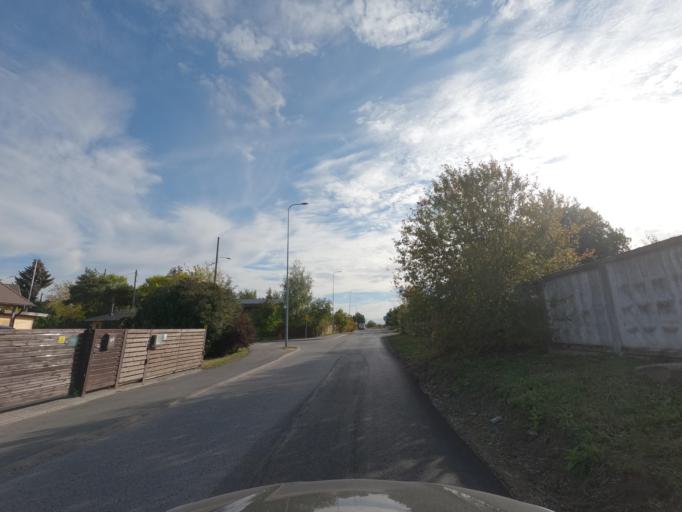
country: EE
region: Harju
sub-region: Saue vald
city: Laagri
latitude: 59.3482
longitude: 24.6305
